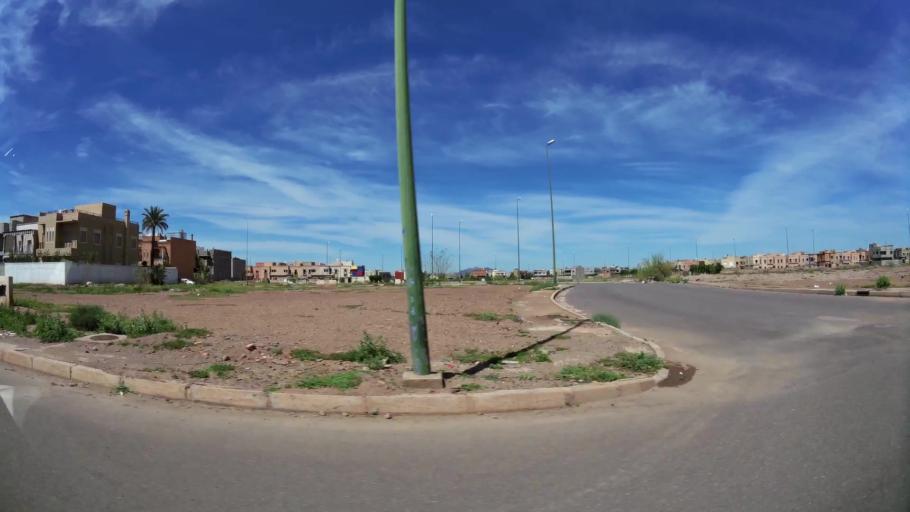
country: MA
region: Marrakech-Tensift-Al Haouz
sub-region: Marrakech
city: Marrakesh
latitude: 31.6497
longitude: -8.0765
